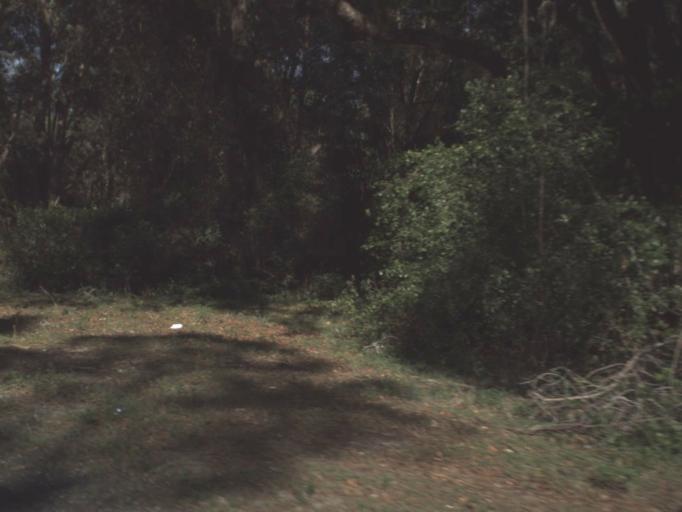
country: US
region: Florida
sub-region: Marion County
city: Dunnellon
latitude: 29.1180
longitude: -82.4384
